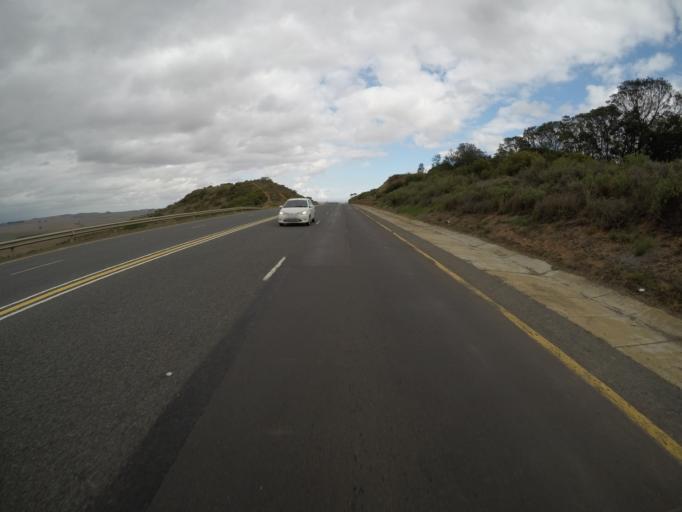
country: ZA
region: Western Cape
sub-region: Overberg District Municipality
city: Swellendam
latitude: -34.0974
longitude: 20.7338
